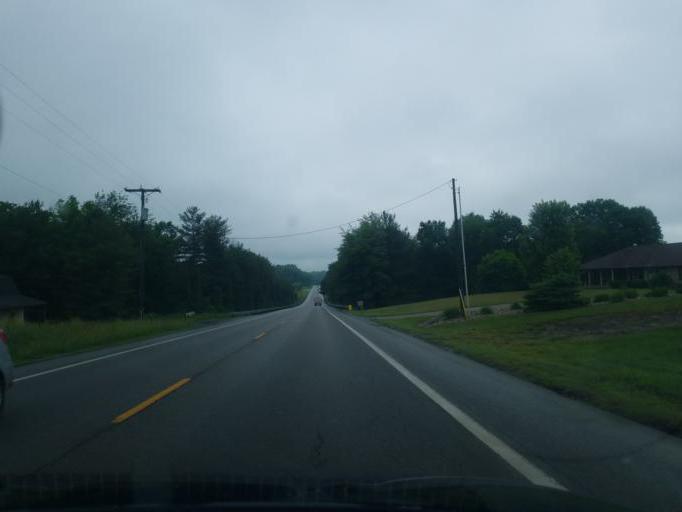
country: US
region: Ohio
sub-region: Tuscarawas County
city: Sugarcreek
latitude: 40.5189
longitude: -81.6927
